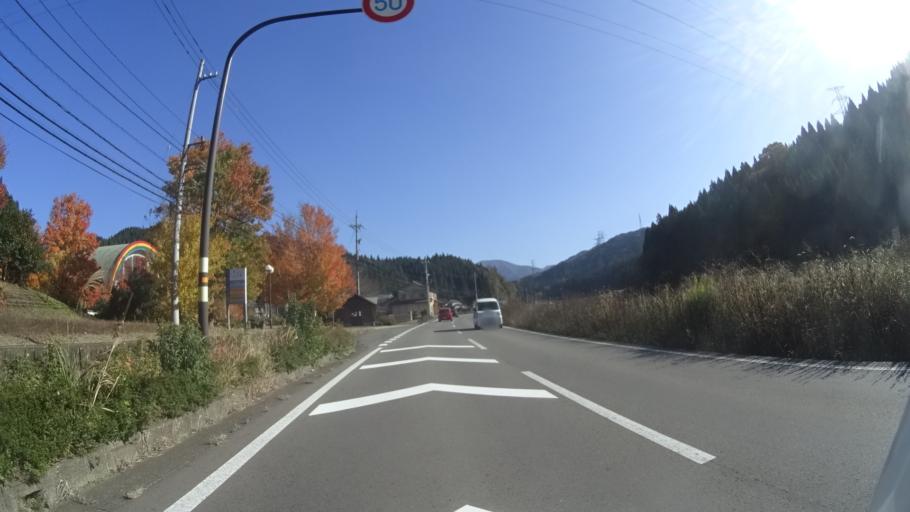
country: JP
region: Fukui
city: Ono
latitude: 36.0048
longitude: 136.4018
